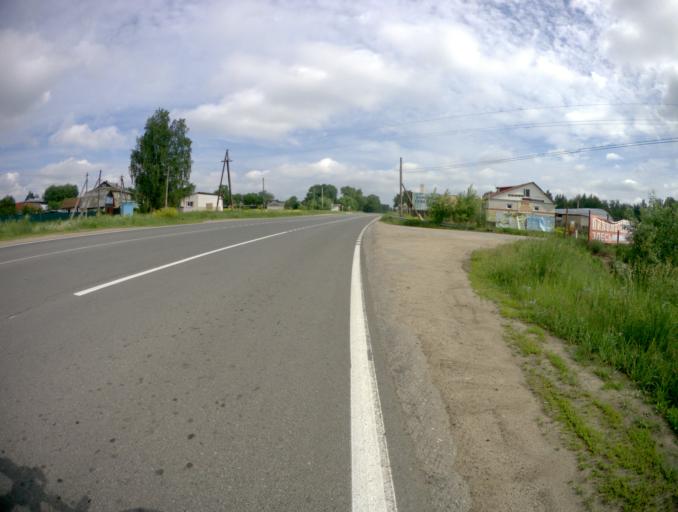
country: RU
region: Vladimir
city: Lakinsk
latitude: 56.0387
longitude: 39.9763
